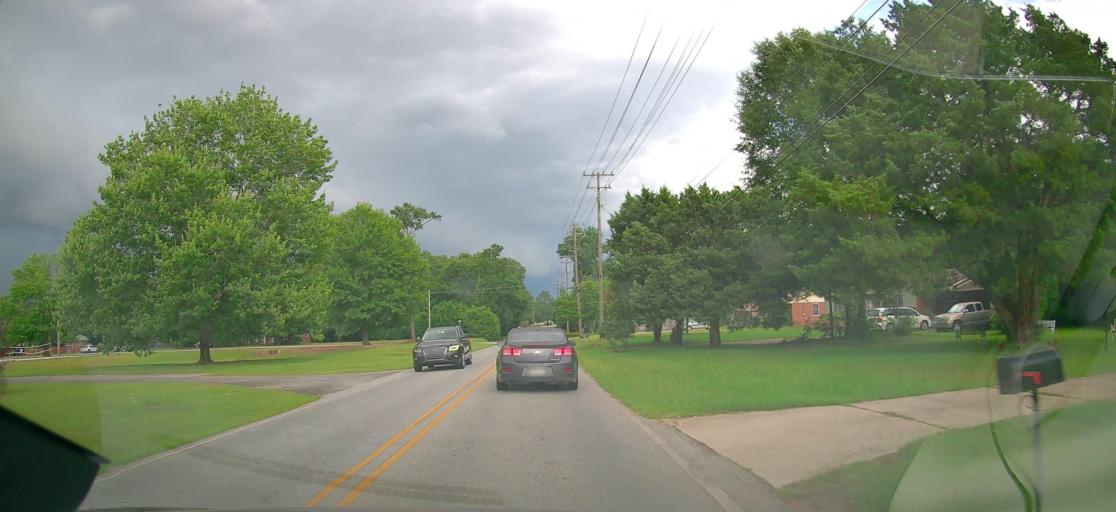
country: US
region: Georgia
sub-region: Houston County
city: Centerville
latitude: 32.6317
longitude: -83.6886
